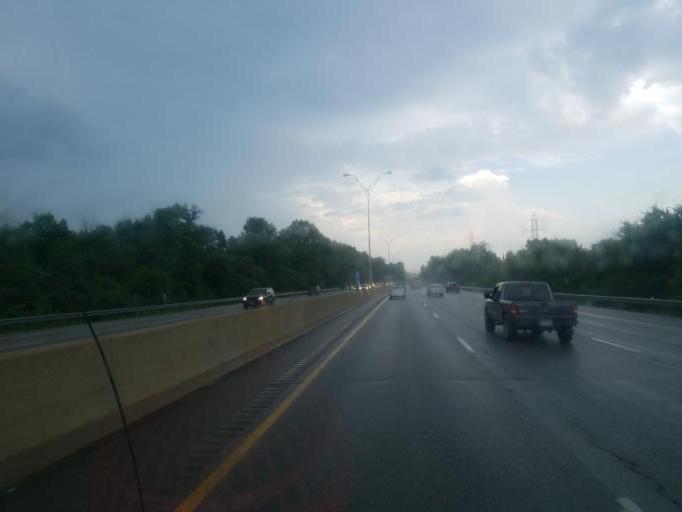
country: US
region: Ohio
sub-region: Summit County
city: Portage Lakes
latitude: 41.0247
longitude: -81.5159
